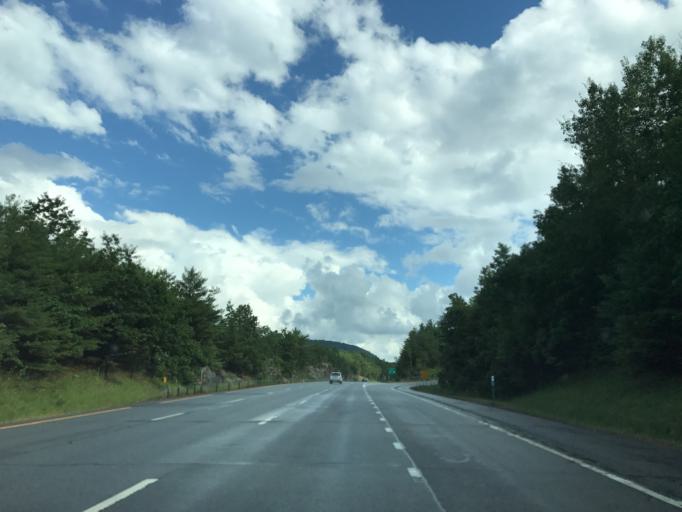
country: US
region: New York
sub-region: Warren County
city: Glens Falls North
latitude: 43.4070
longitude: -73.7176
